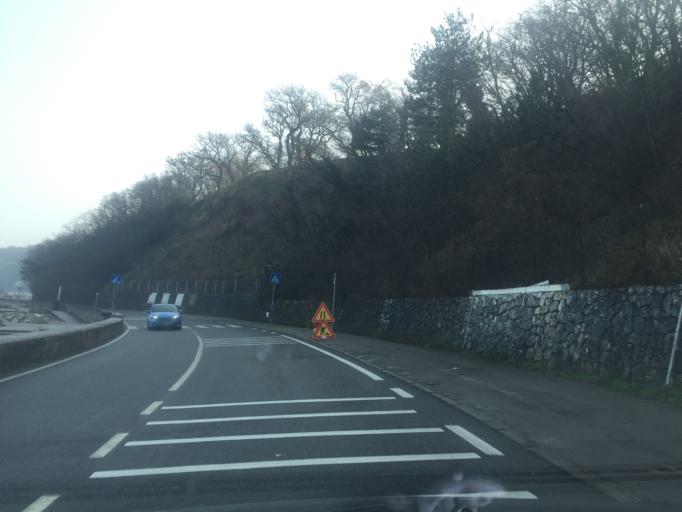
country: SI
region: Koper-Capodistria
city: Ankaran
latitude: 45.6053
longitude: 13.7215
